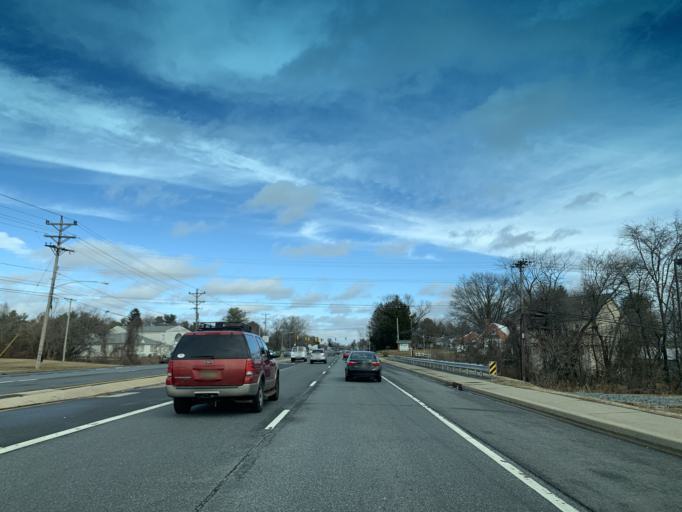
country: US
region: Delaware
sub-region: New Castle County
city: Pike Creek
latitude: 39.7080
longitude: -75.6832
